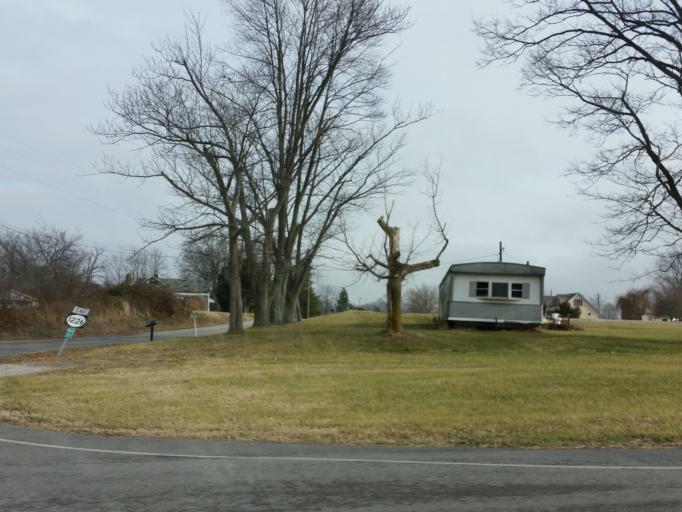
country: US
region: Kentucky
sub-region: Trimble County
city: Bedford
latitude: 38.6605
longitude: -85.3191
